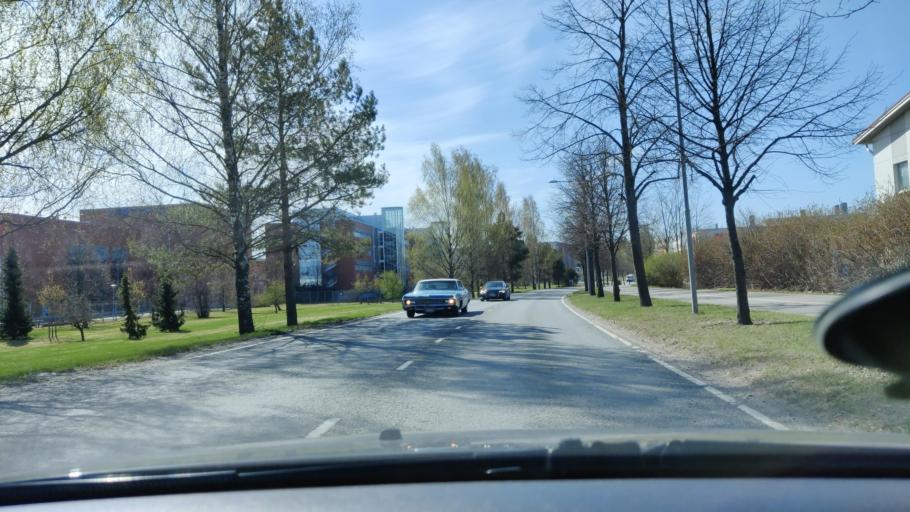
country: FI
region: Uusimaa
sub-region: Helsinki
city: Kerava
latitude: 60.3841
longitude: 25.1093
